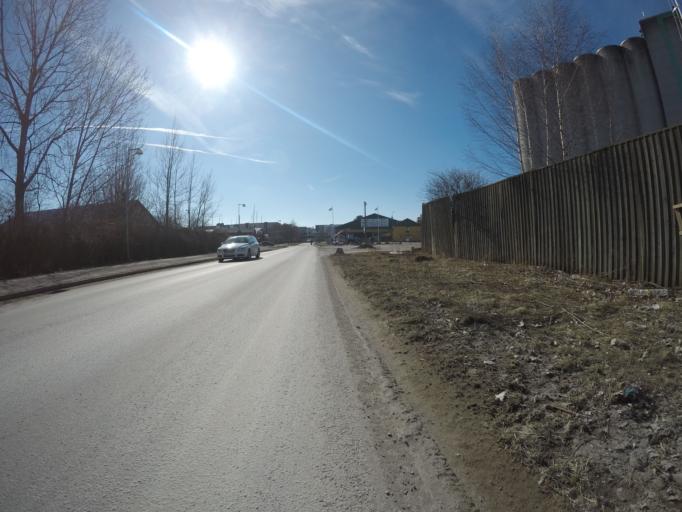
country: SE
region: Vaestmanland
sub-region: Vasteras
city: Vasteras
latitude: 59.6077
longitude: 16.5610
